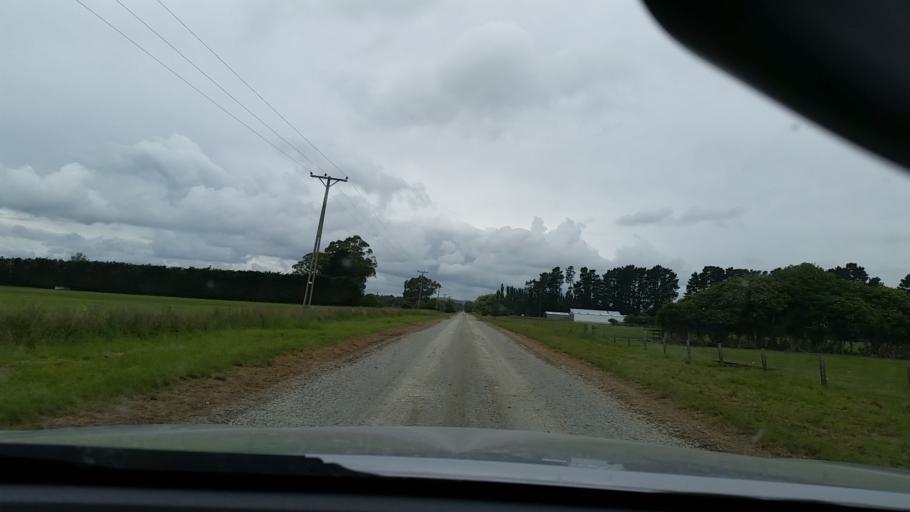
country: NZ
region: Southland
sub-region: Southland District
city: Winton
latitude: -46.1837
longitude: 168.2887
